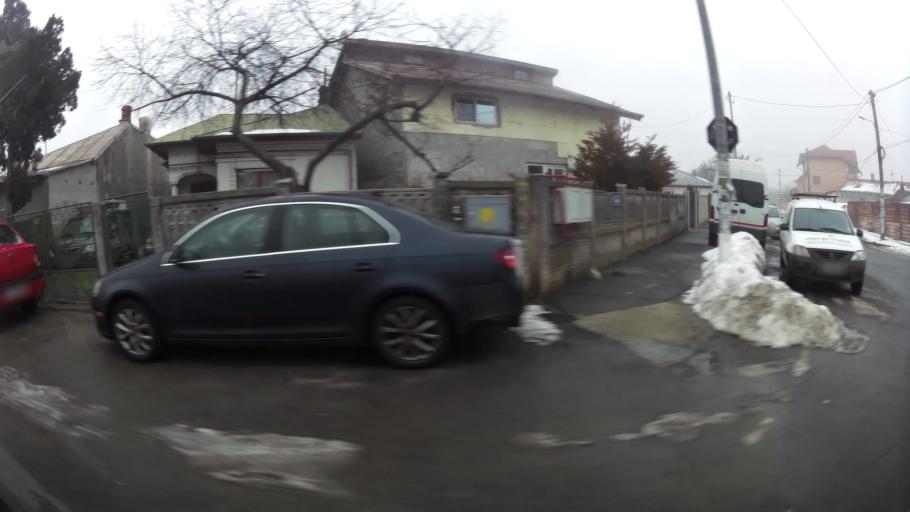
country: RO
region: Ilfov
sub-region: Comuna Chiajna
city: Chiajna
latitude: 44.4570
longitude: 25.9676
